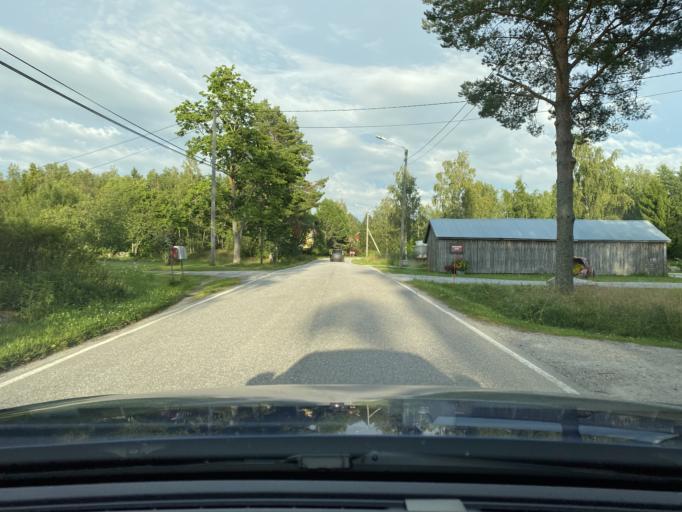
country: FI
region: Ostrobothnia
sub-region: Vaasa
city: Korsnaes
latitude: 62.9718
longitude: 21.1814
